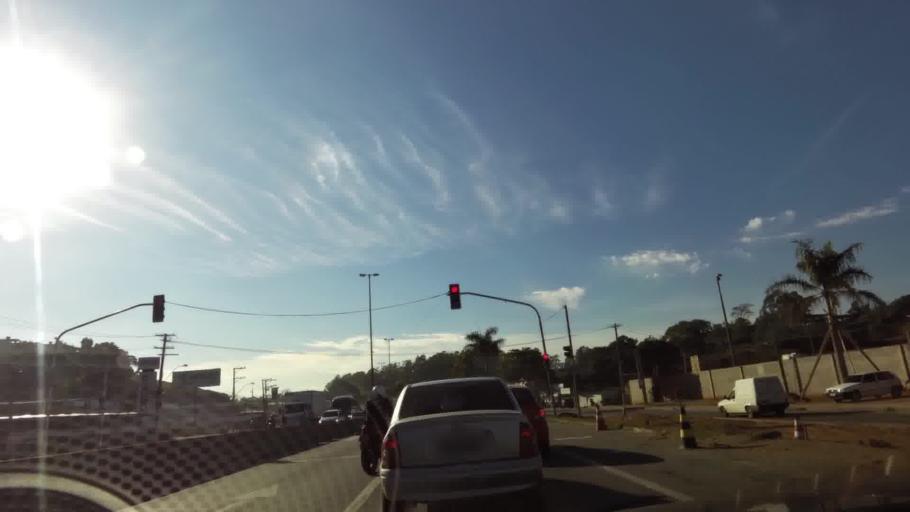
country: BR
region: Espirito Santo
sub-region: Viana
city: Viana
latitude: -20.3582
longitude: -40.4254
